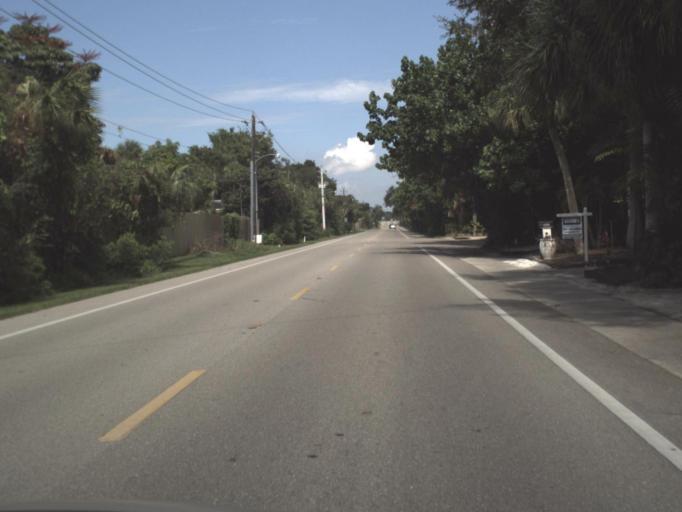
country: US
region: Florida
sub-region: Sarasota County
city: South Sarasota
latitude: 27.2793
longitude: -82.5509
